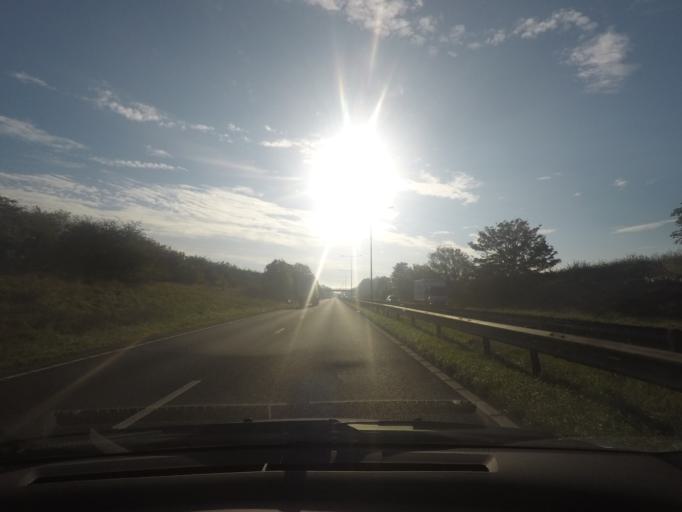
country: GB
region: England
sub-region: East Riding of Yorkshire
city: Brantingham
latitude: 53.7525
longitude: -0.5804
